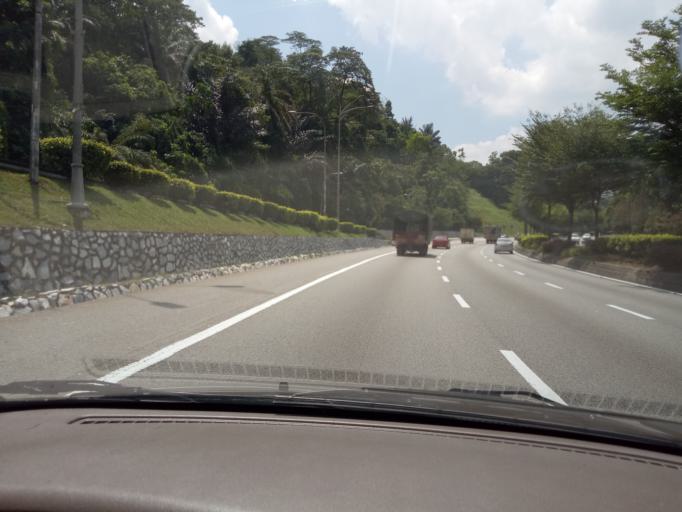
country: MY
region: Kuala Lumpur
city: Kuala Lumpur
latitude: 3.1584
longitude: 101.6813
